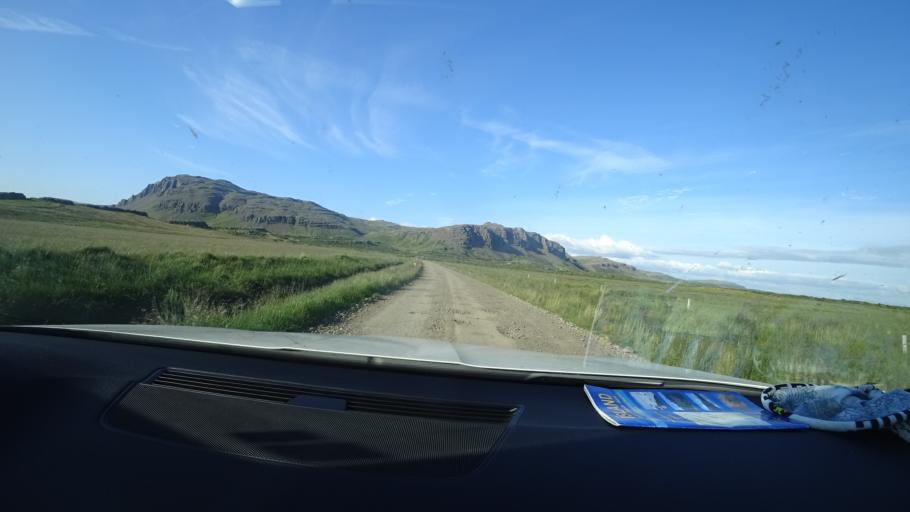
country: IS
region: West
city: Borgarnes
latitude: 64.6868
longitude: -21.9435
